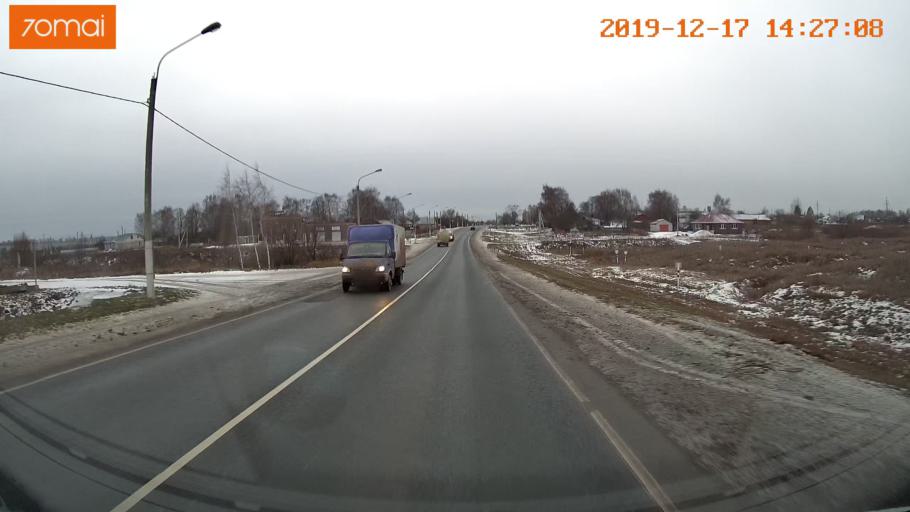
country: RU
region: Rjazan
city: Zakharovo
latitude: 54.3771
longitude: 39.2963
